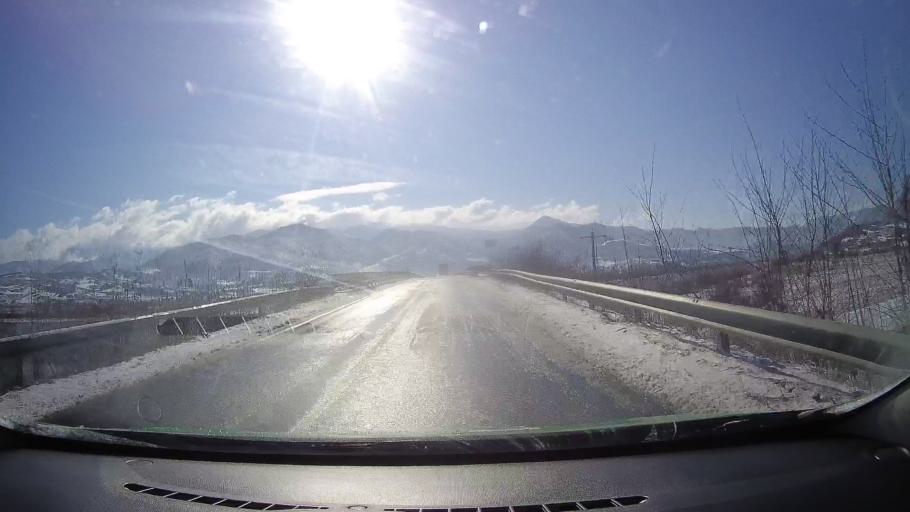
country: RO
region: Sibiu
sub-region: Comuna Turnu Rosu
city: Turnu Rosu
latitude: 45.6557
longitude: 24.2976
